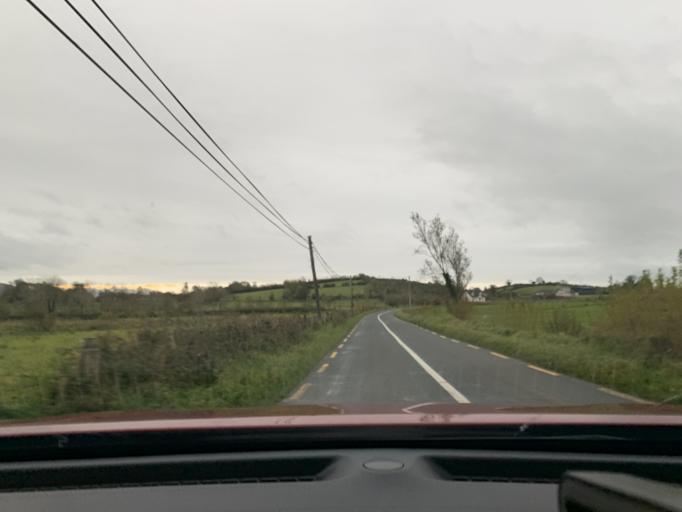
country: IE
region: Connaught
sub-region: Sligo
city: Ballymote
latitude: 54.0717
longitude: -8.5091
